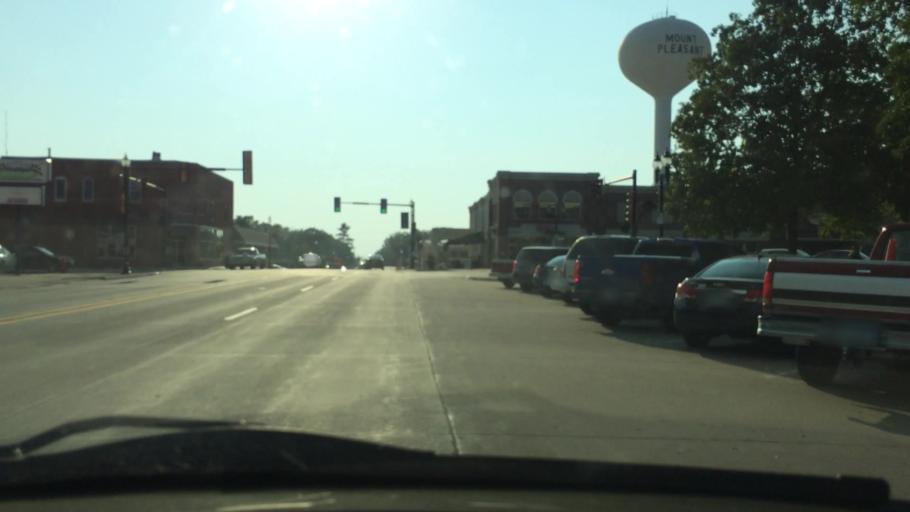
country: US
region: Iowa
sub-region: Henry County
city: Mount Pleasant
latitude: 40.9656
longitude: -91.5541
